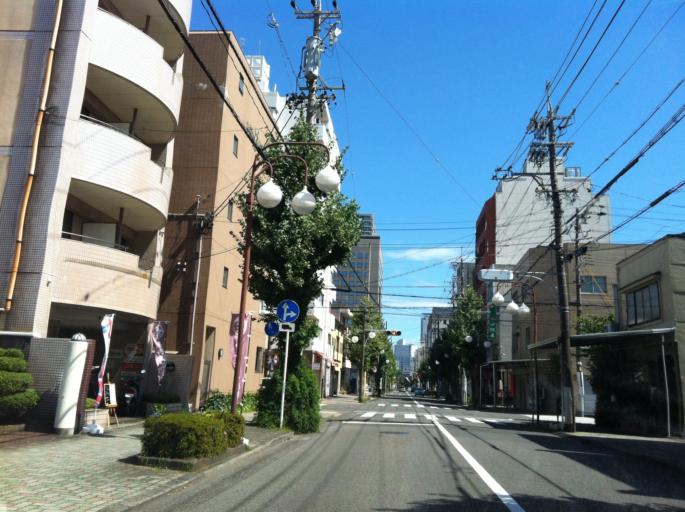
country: JP
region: Shizuoka
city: Shizuoka-shi
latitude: 34.9773
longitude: 138.3758
